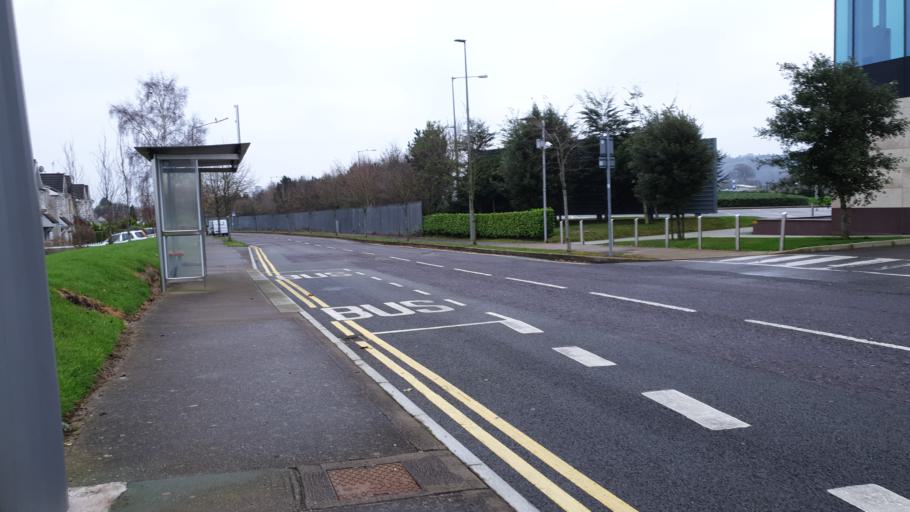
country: IE
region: Munster
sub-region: County Cork
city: Passage West
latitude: 51.8872
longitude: -8.4021
